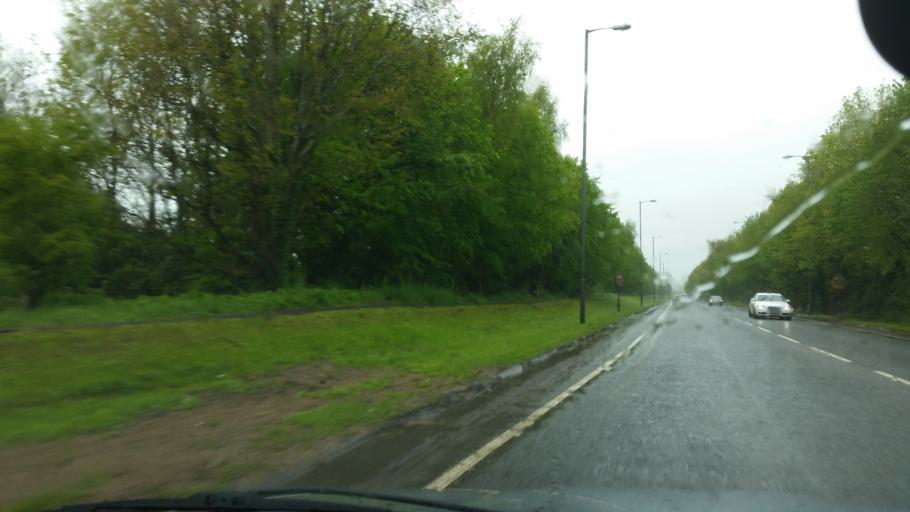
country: GB
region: Northern Ireland
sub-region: Strabane District
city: Strabane
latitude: 54.8317
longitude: -7.4692
